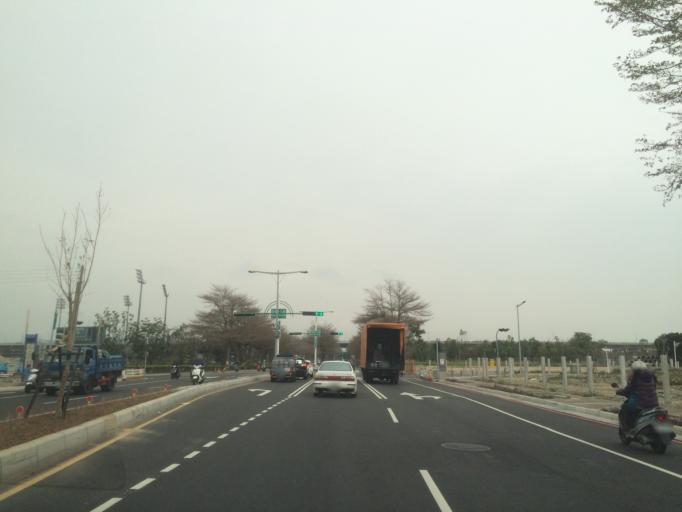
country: TW
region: Taiwan
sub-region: Taichung City
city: Taichung
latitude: 24.1972
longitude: 120.6866
